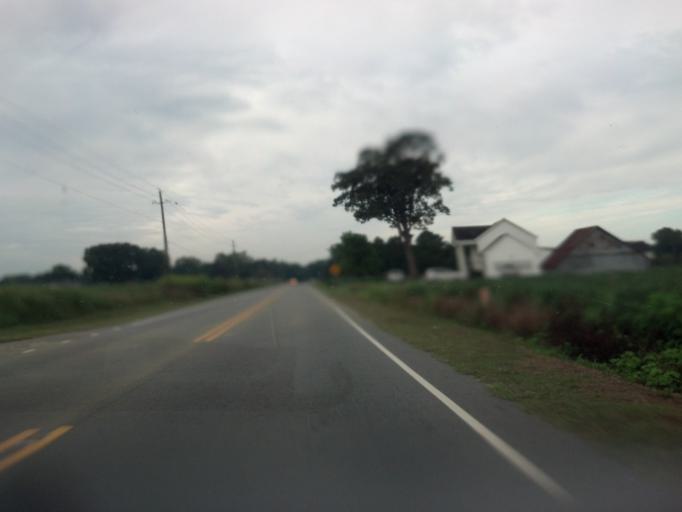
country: US
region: North Carolina
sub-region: Pitt County
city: Ayden
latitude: 35.4763
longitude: -77.4626
